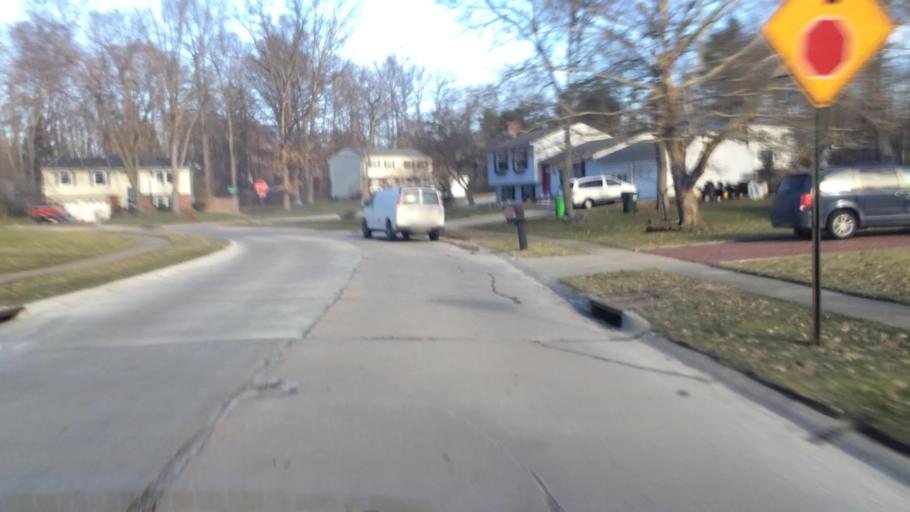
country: US
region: Ohio
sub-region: Summit County
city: Silver Lake
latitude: 41.1783
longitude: -81.4564
